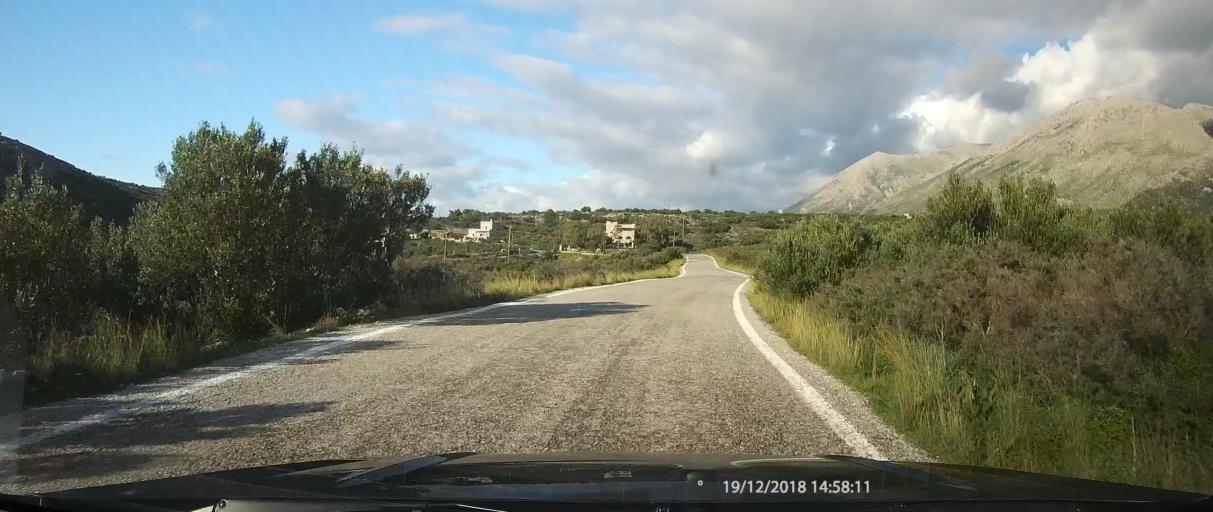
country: GR
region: Peloponnese
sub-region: Nomos Lakonias
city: Gytheio
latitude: 36.4864
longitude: 22.4027
